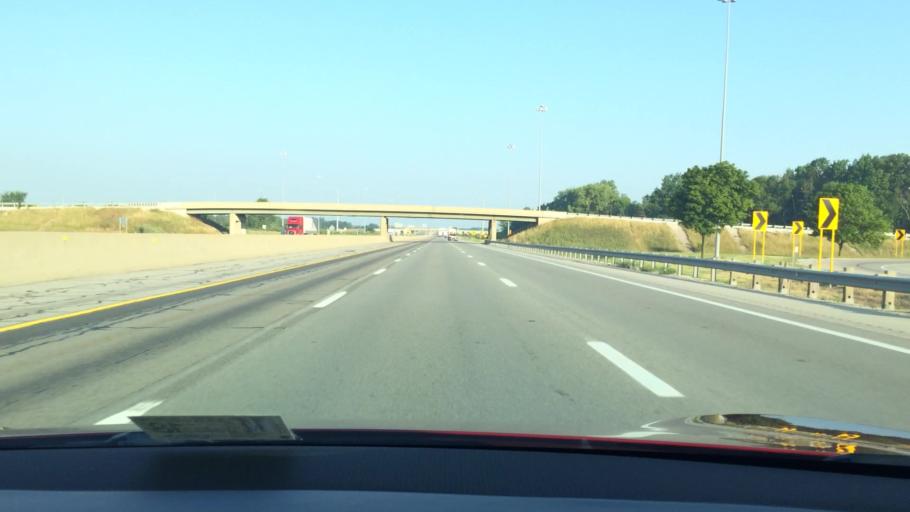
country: US
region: Ohio
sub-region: Sandusky County
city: Fremont
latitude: 41.4009
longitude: -83.1105
